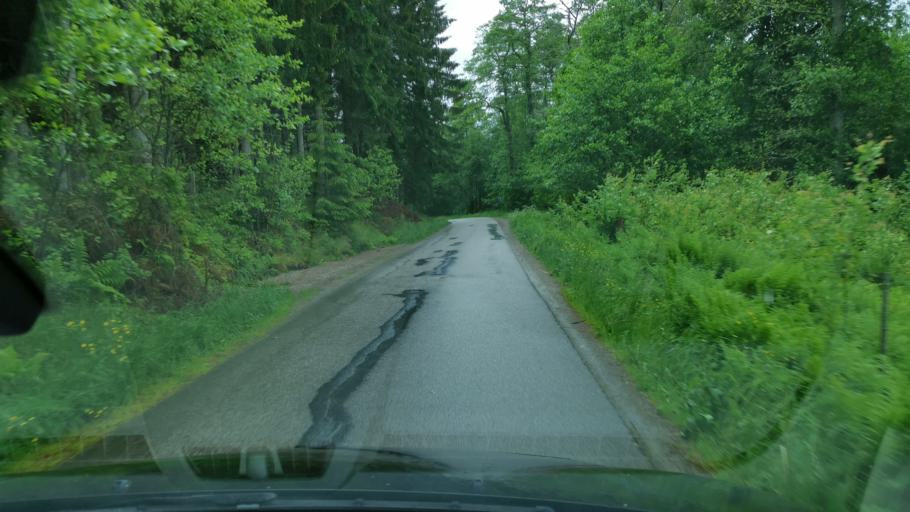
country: SE
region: Vaestra Goetaland
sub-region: Orust
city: Henan
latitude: 58.3281
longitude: 11.7188
